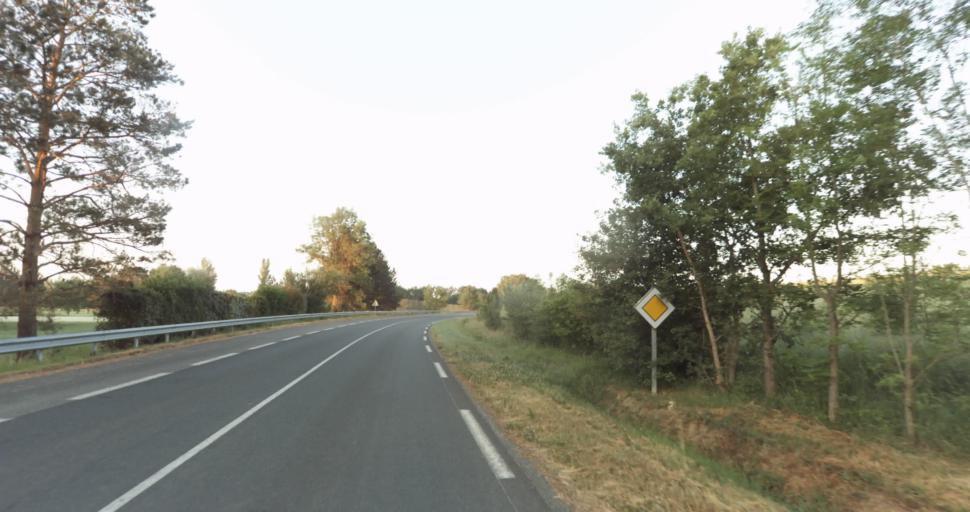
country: FR
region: Midi-Pyrenees
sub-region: Departement du Gers
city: Pujaudran
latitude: 43.6402
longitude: 1.1077
